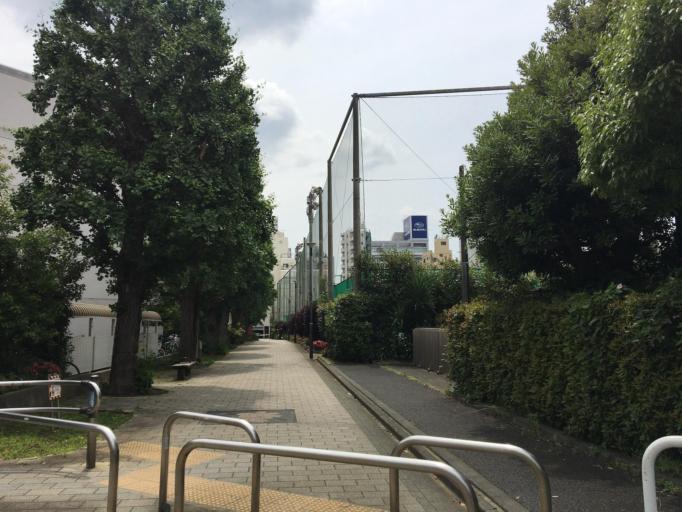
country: JP
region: Tokyo
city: Tokyo
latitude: 35.6199
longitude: 139.7138
